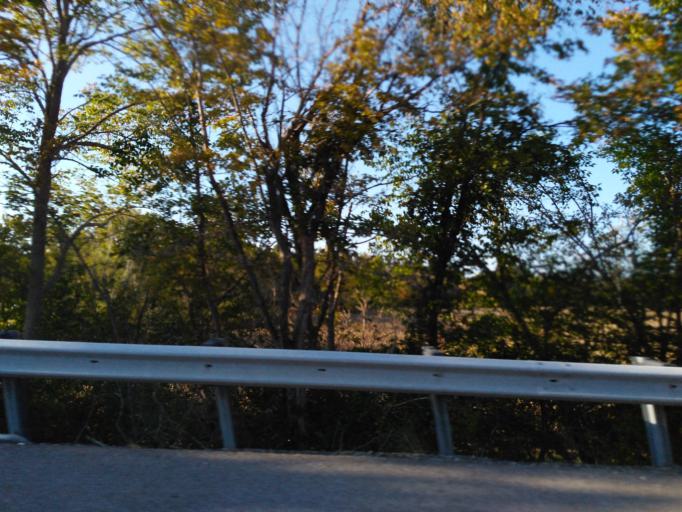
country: US
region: Illinois
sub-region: Madison County
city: Maryville
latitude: 38.7145
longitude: -89.9278
